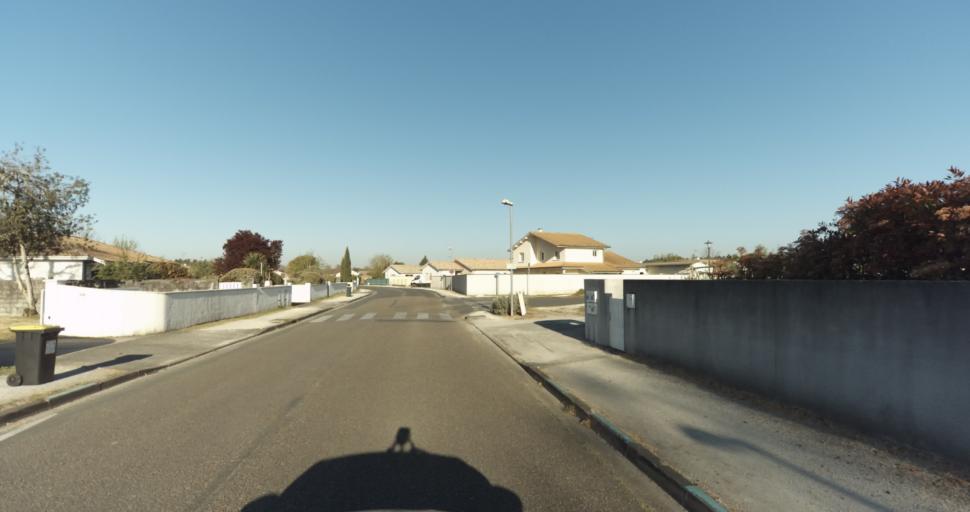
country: FR
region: Aquitaine
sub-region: Departement de la Gironde
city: Martignas-sur-Jalle
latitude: 44.8131
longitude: -0.7866
